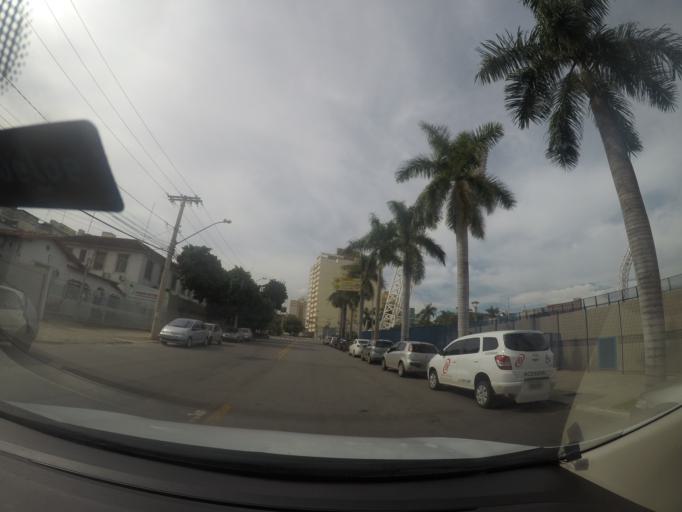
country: BR
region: Goias
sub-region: Goiania
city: Goiania
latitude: -16.6706
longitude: -49.2616
